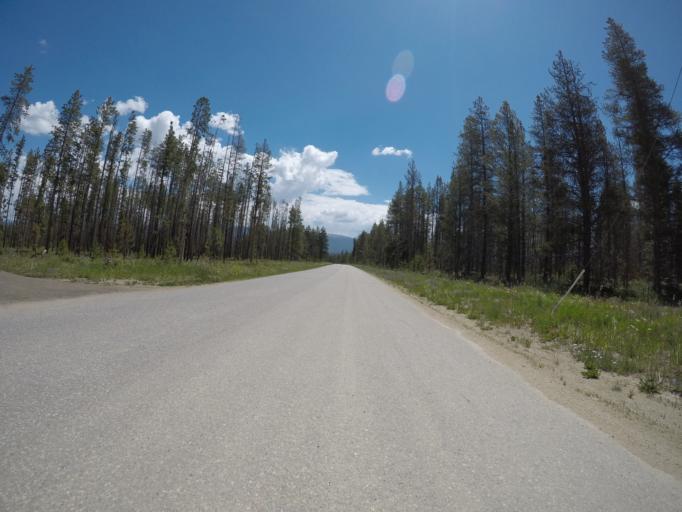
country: US
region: Colorado
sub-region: Grand County
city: Fraser
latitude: 39.9469
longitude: -105.8483
